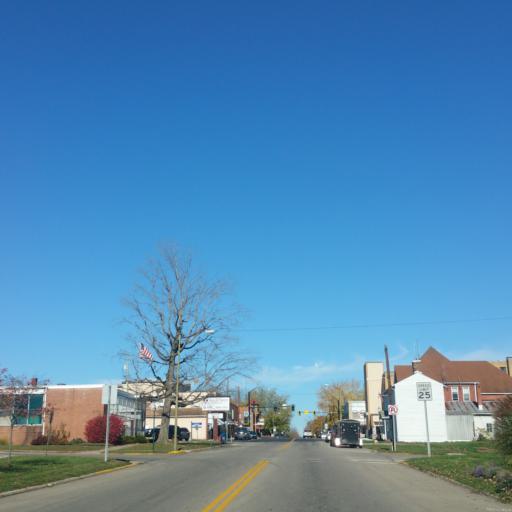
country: US
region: Ohio
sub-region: Vinton County
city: McArthur
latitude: 39.2450
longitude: -82.4791
